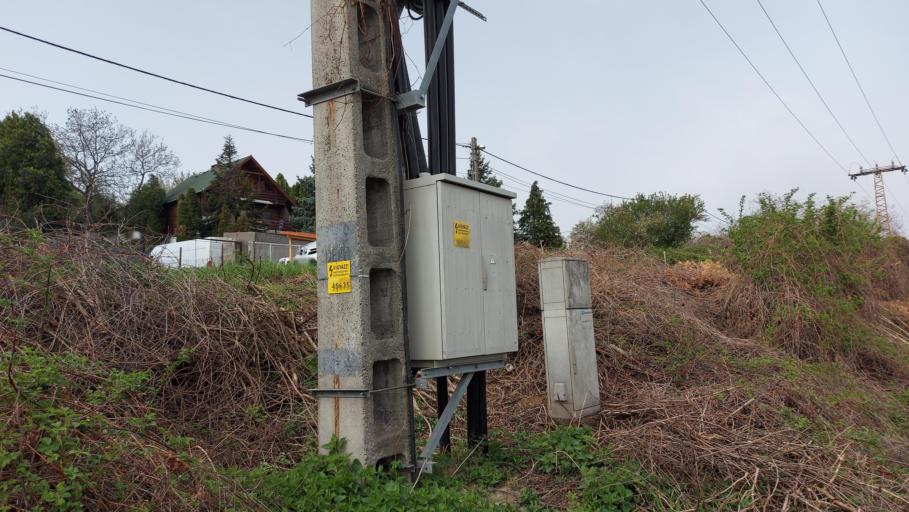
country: HU
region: Pest
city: Budaors
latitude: 47.4381
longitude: 18.9478
